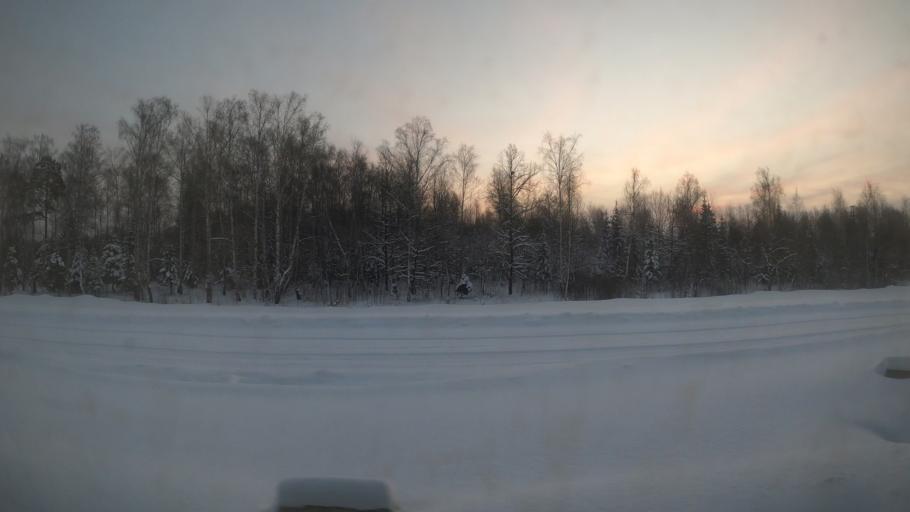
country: RU
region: Moskovskaya
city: Lugovaya
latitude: 56.0310
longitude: 37.4876
